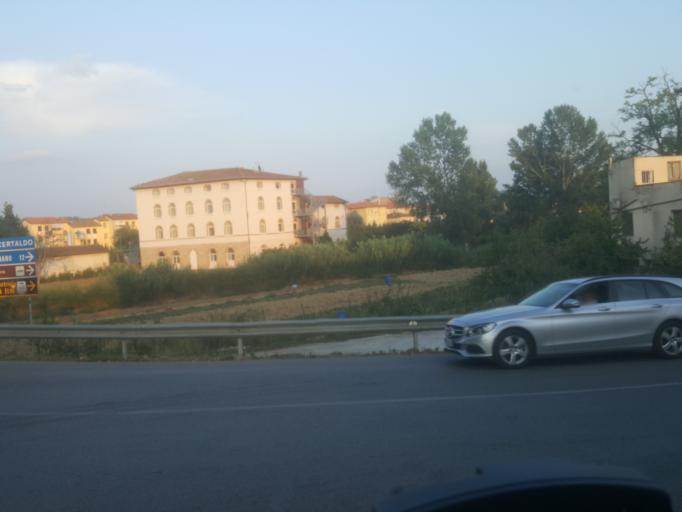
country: IT
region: Tuscany
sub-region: Province of Florence
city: Certaldo
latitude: 43.5445
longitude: 11.0336
